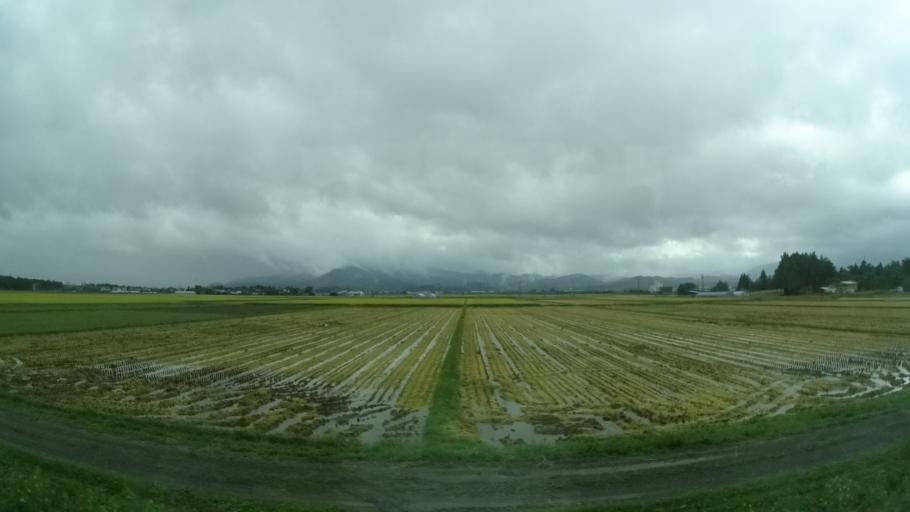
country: JP
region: Yamagata
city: Tsuruoka
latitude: 38.7425
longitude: 139.7864
